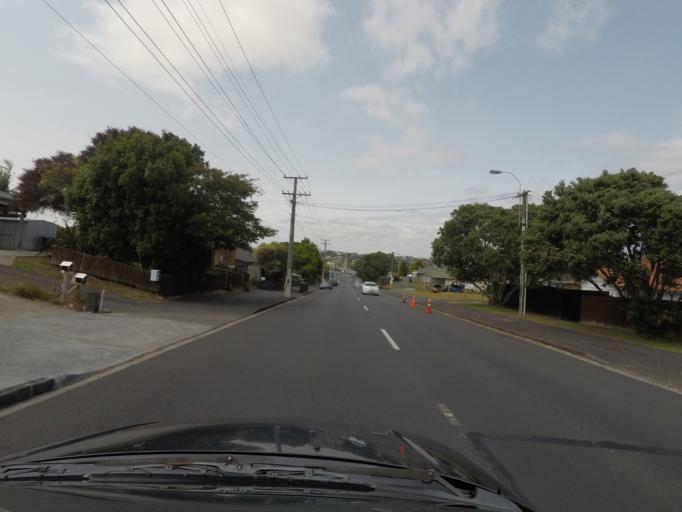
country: NZ
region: Auckland
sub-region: Auckland
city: Rosebank
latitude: -36.9036
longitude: 174.7016
